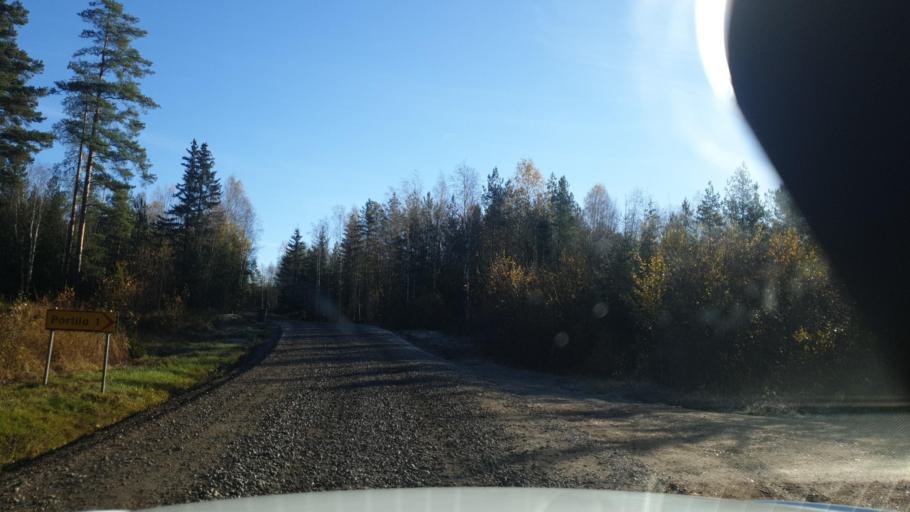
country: SE
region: Vaermland
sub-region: Karlstads Kommun
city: Valberg
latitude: 59.4164
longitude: 13.1252
